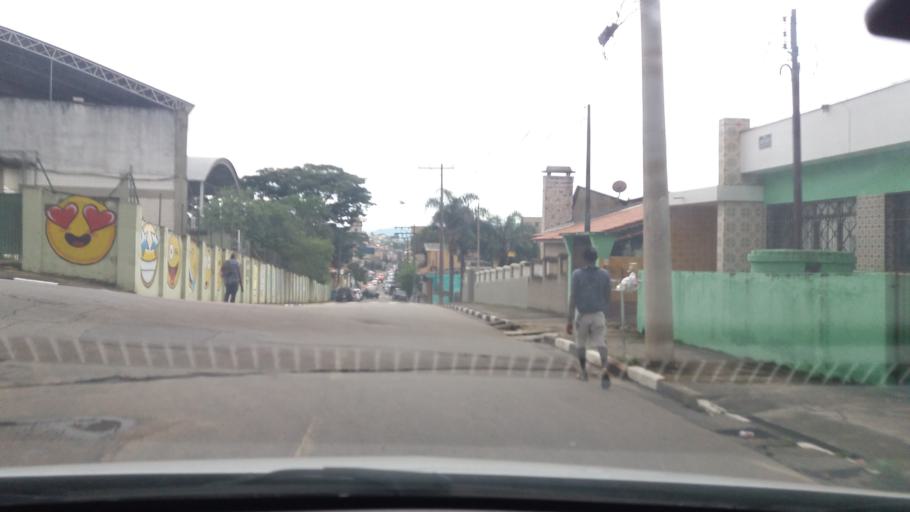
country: BR
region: Sao Paulo
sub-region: Bom Jesus Dos Perdoes
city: Bom Jesus dos Perdoes
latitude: -23.1378
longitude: -46.4630
